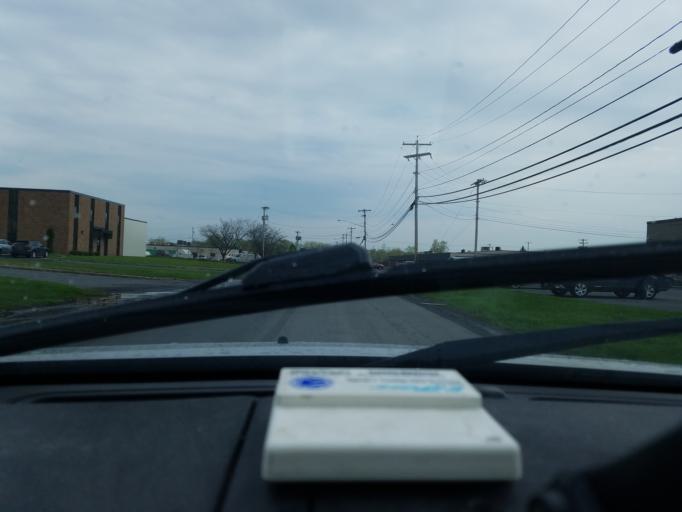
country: US
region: New York
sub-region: Onondaga County
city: East Syracuse
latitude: 43.1028
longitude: -76.0854
